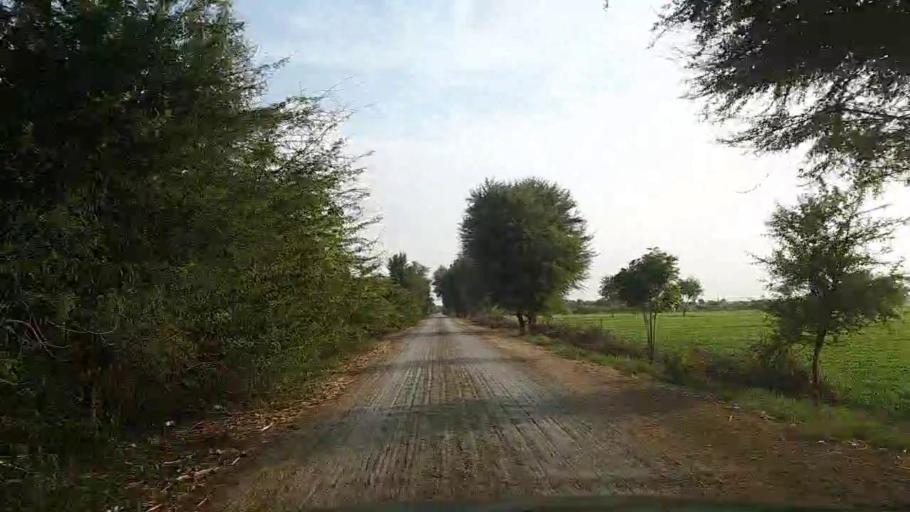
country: PK
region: Sindh
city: Jam Sahib
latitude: 26.4374
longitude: 68.5716
